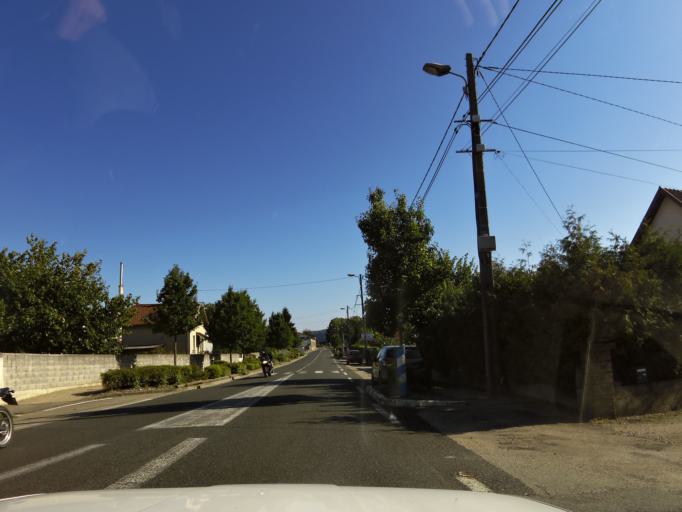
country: FR
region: Rhone-Alpes
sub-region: Departement de l'Ain
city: Lagnieu
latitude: 45.9117
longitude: 5.3453
